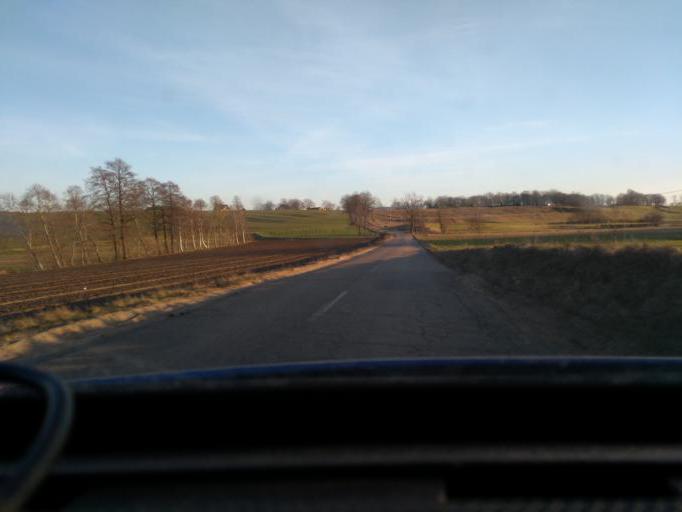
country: PL
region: Pomeranian Voivodeship
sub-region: Powiat kartuski
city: Przodkowo
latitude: 54.4075
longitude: 18.3278
